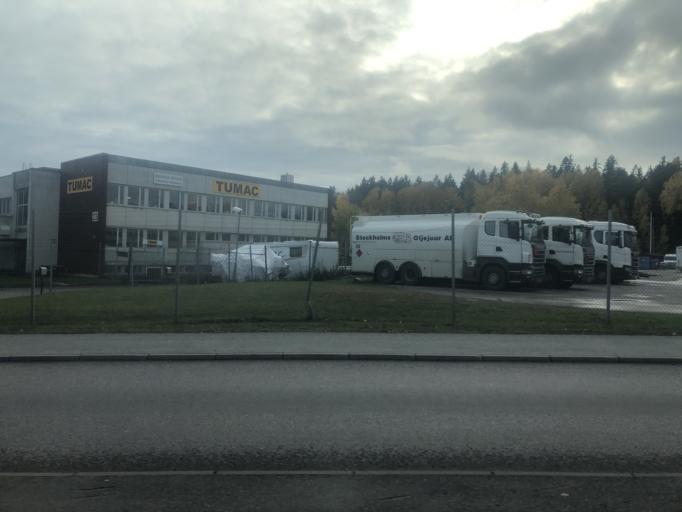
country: SE
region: Stockholm
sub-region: Jarfalla Kommun
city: Jakobsberg
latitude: 59.4063
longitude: 17.8428
